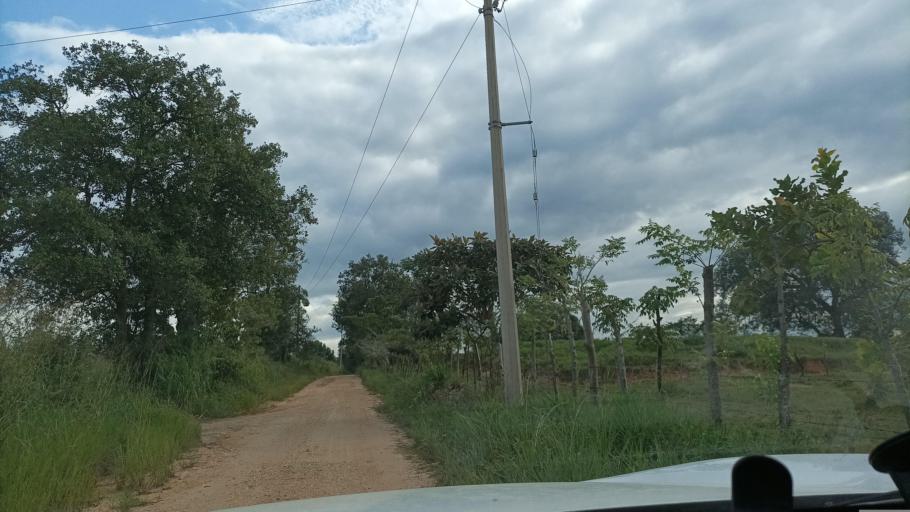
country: MX
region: Veracruz
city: Oluta
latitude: 17.9389
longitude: -94.8821
